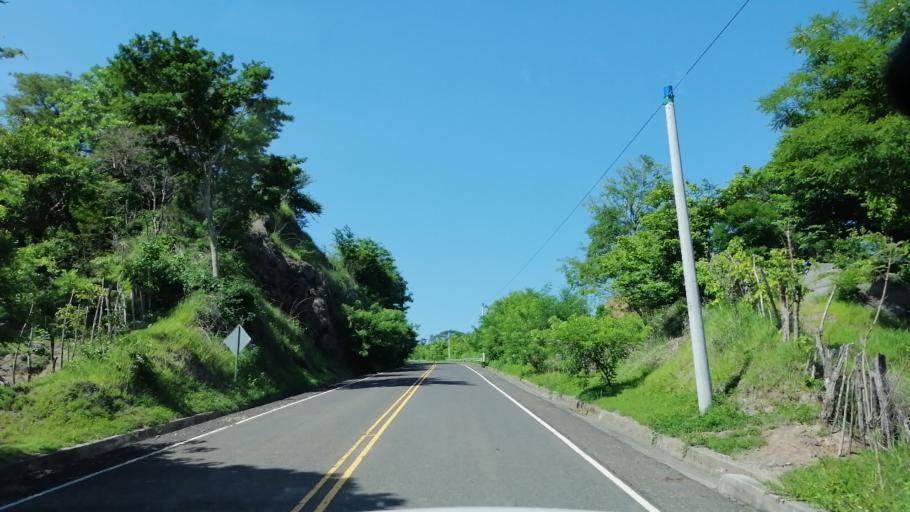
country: HN
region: Lempira
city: La Virtud
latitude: 13.9763
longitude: -88.7633
